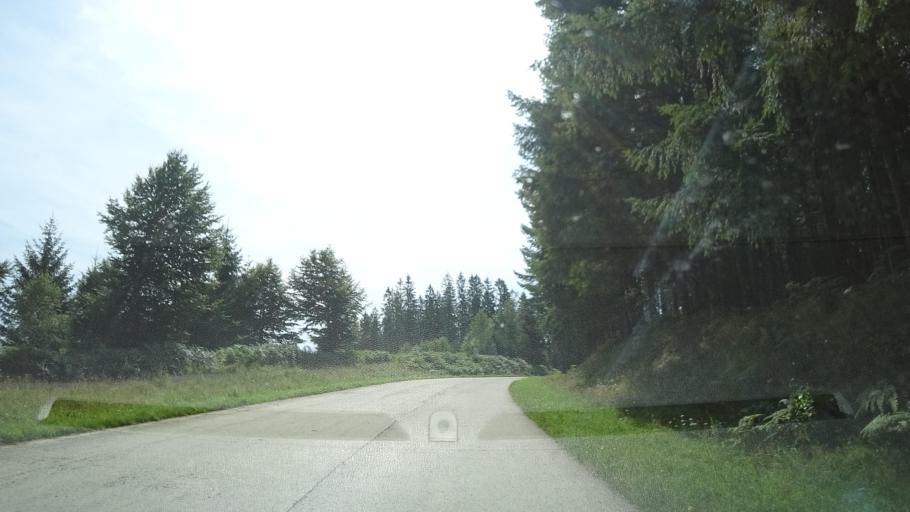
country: BE
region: Wallonia
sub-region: Province du Luxembourg
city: Herbeumont
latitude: 49.7958
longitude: 5.2572
